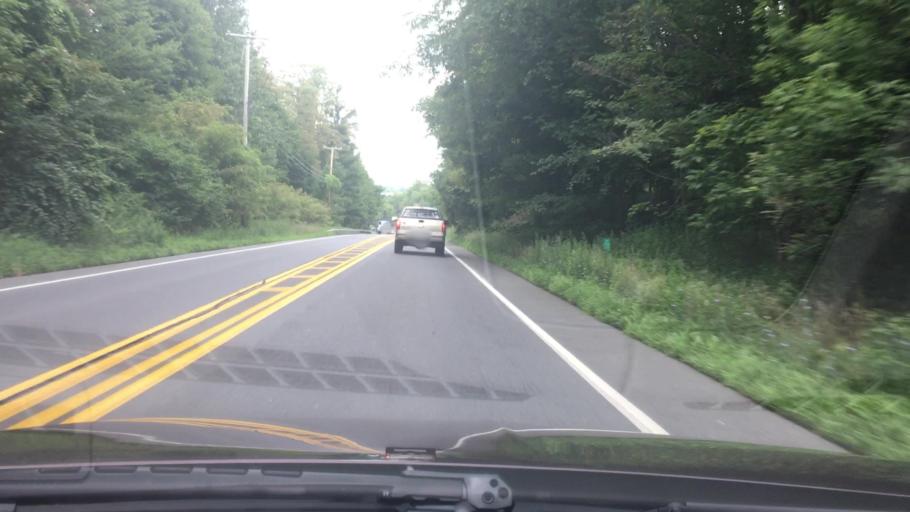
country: US
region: New York
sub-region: Dutchess County
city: Hillside Lake
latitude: 41.6497
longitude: -73.7279
